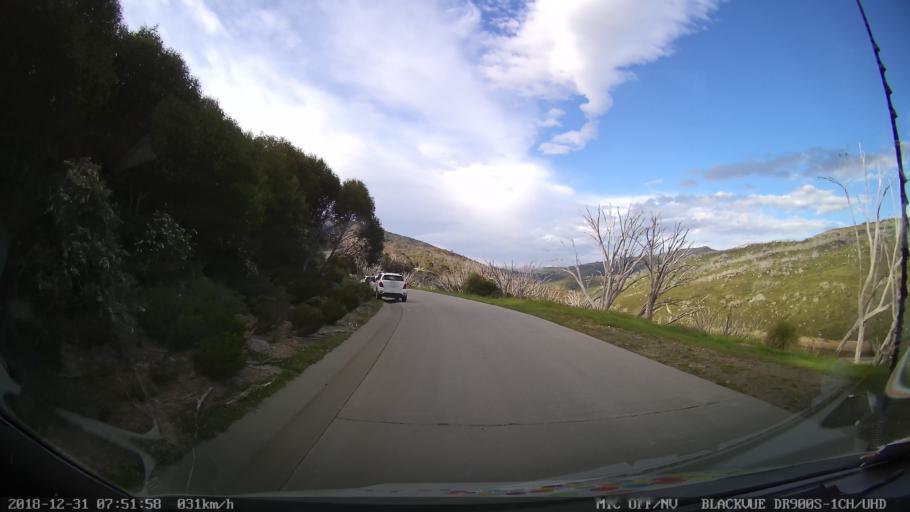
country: AU
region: New South Wales
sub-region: Snowy River
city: Jindabyne
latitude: -36.3786
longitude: 148.3741
